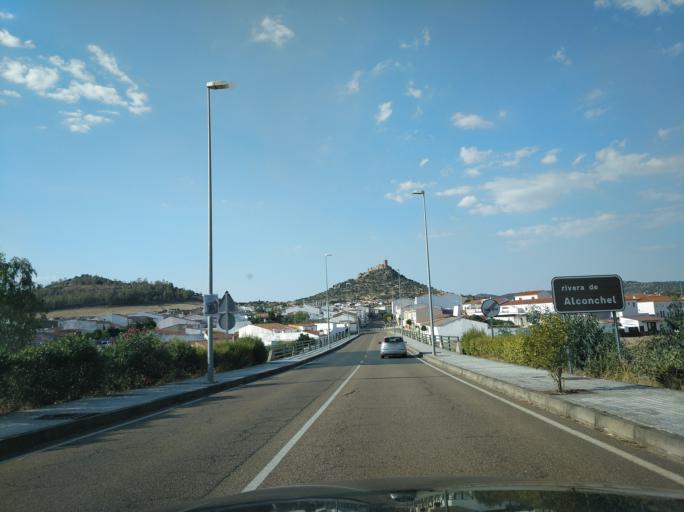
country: ES
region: Extremadura
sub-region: Provincia de Badajoz
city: Alconchel
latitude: 38.5115
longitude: -7.0699
